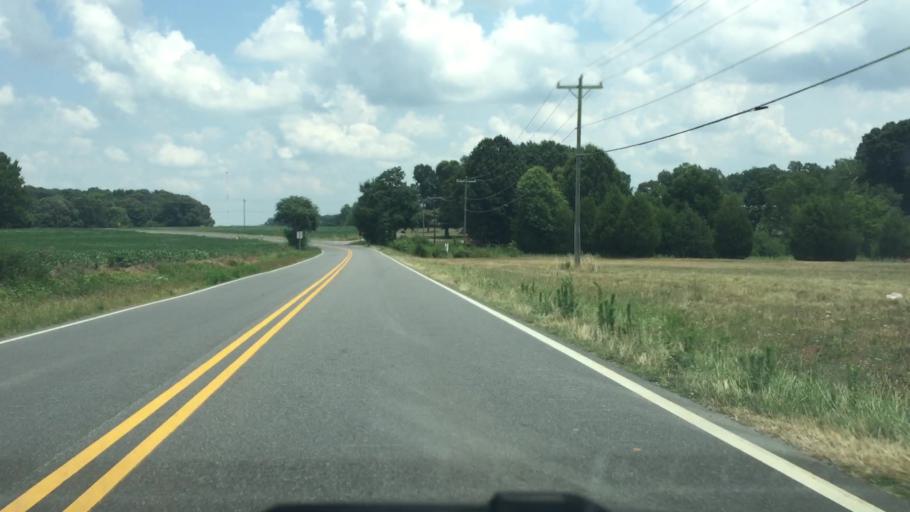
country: US
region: North Carolina
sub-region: Iredell County
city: Troutman
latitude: 35.7185
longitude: -80.8773
